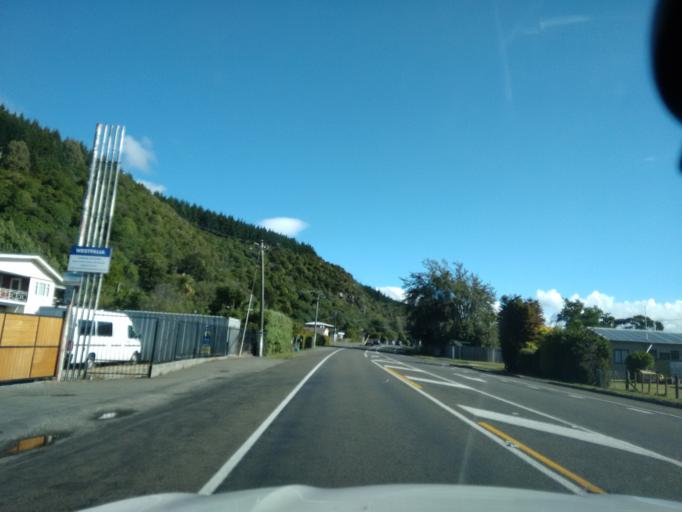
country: NZ
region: Waikato
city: Turangi
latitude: -38.9318
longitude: 175.8763
